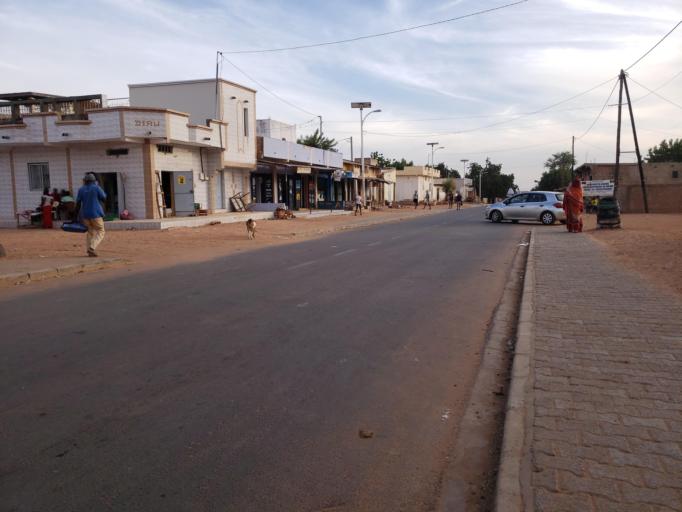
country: SN
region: Louga
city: Ndibene Dahra
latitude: 15.3960
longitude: -15.1203
